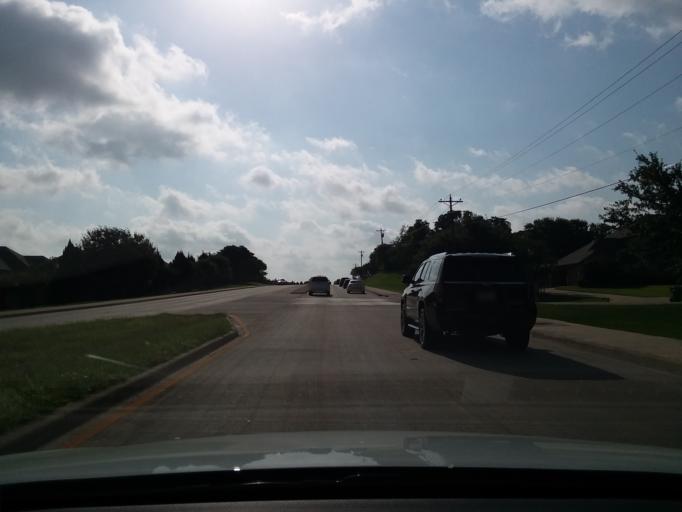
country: US
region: Texas
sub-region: Denton County
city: Bartonville
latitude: 33.0739
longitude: -97.1201
